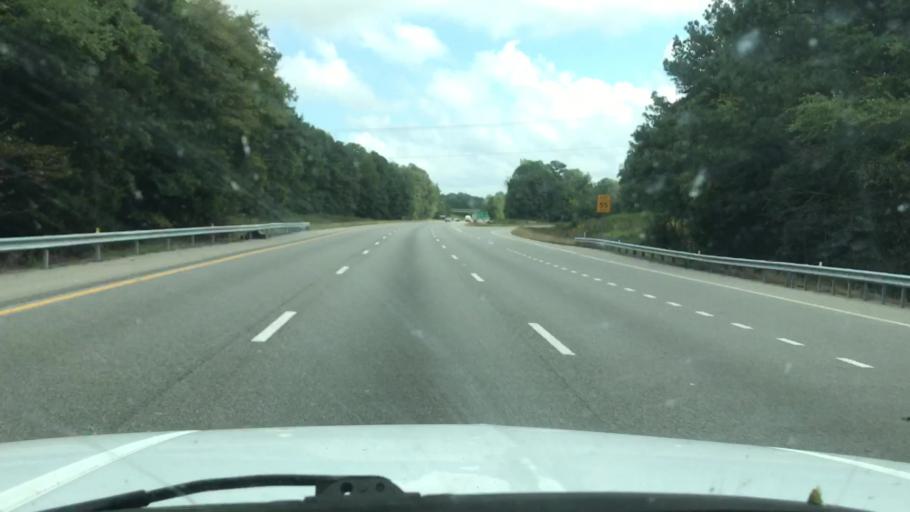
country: US
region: Virginia
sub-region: Henrico County
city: Short Pump
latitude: 37.6675
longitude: -77.5893
